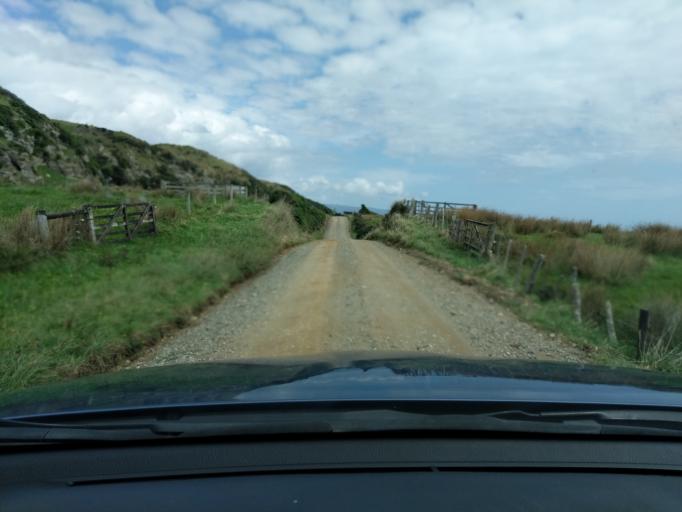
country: NZ
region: Tasman
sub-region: Tasman District
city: Takaka
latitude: -40.6650
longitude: 172.4084
